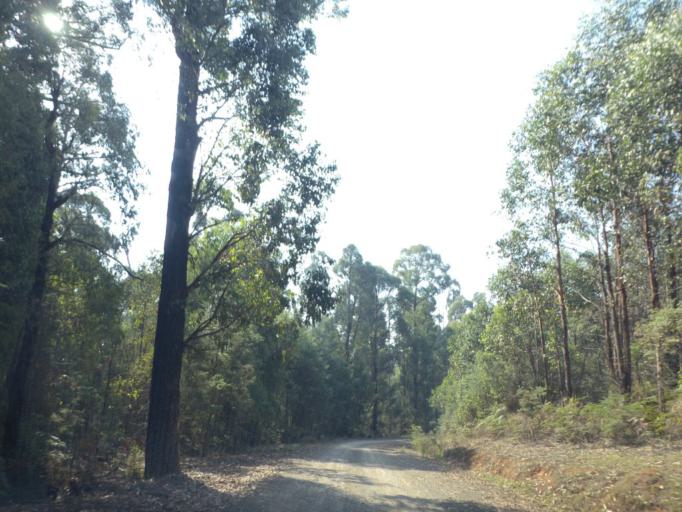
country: AU
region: Victoria
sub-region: Yarra Ranges
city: Millgrove
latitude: -37.5292
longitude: 145.7414
